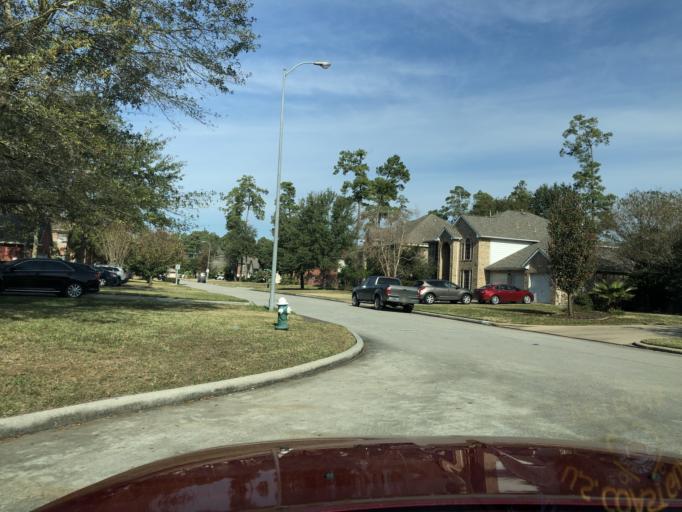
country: US
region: Texas
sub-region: Harris County
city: Tomball
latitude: 30.0253
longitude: -95.5596
